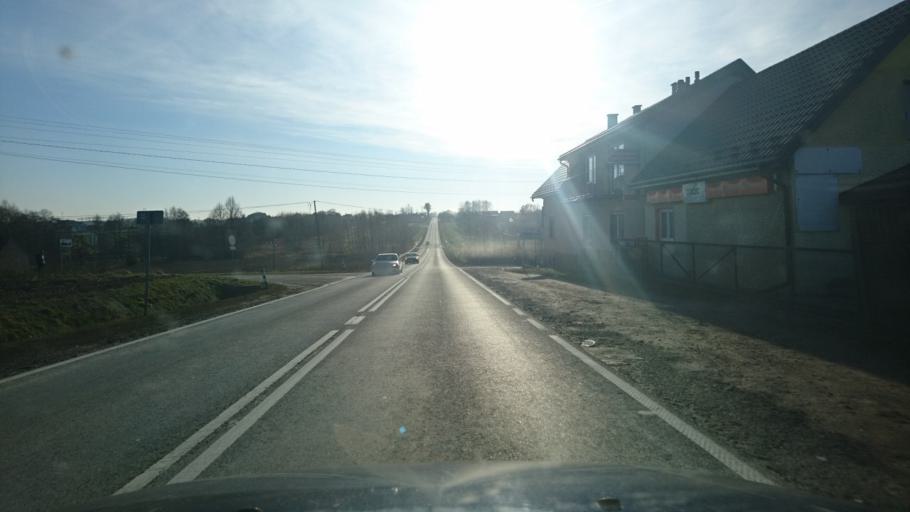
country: PL
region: Opole Voivodeship
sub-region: Powiat oleski
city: Dalachow
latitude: 51.0569
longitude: 18.5991
